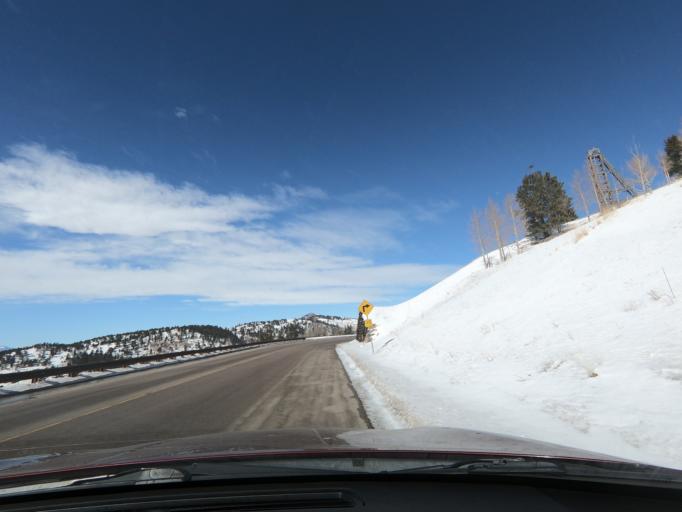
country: US
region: Colorado
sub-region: Teller County
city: Cripple Creek
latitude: 38.7241
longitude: -105.1670
